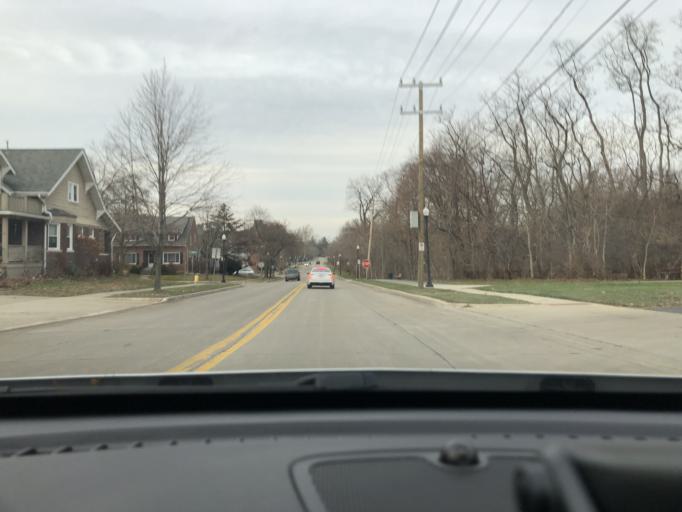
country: US
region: Michigan
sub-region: Wayne County
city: Dearborn Heights
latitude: 42.3088
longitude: -83.2407
